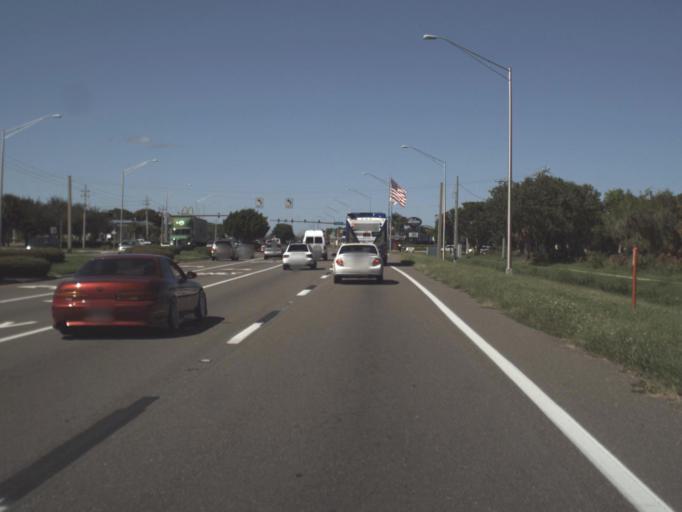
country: US
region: Florida
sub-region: Lee County
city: North Fort Myers
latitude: 26.6622
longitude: -81.8852
